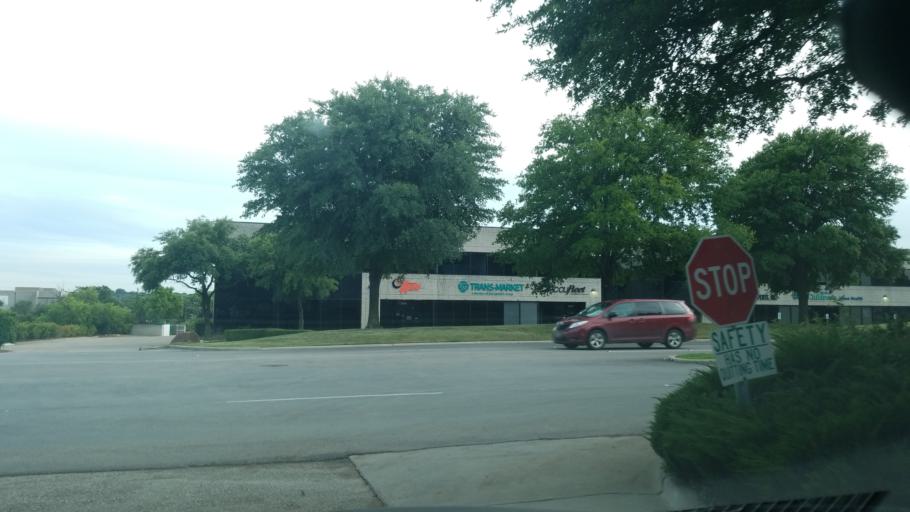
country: US
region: Texas
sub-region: Dallas County
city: Irving
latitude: 32.8716
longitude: -96.9852
